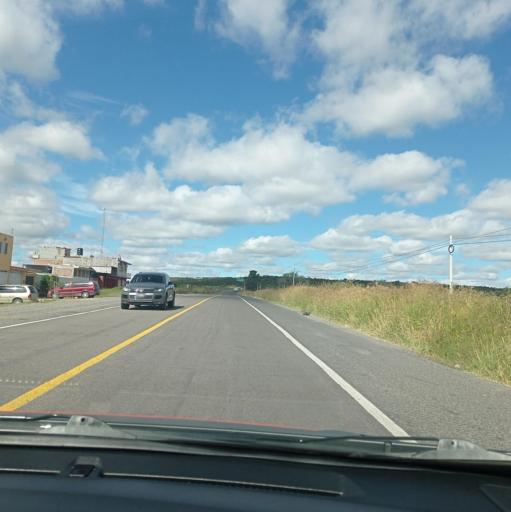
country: MX
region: Jalisco
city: San Diego de Alejandria
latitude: 20.9987
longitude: -102.0020
